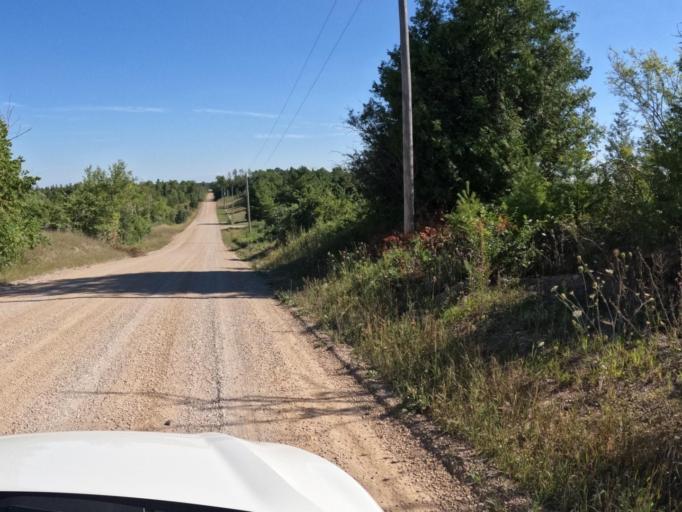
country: CA
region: Ontario
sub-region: Wellington County
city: Guelph
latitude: 43.4223
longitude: -80.1243
